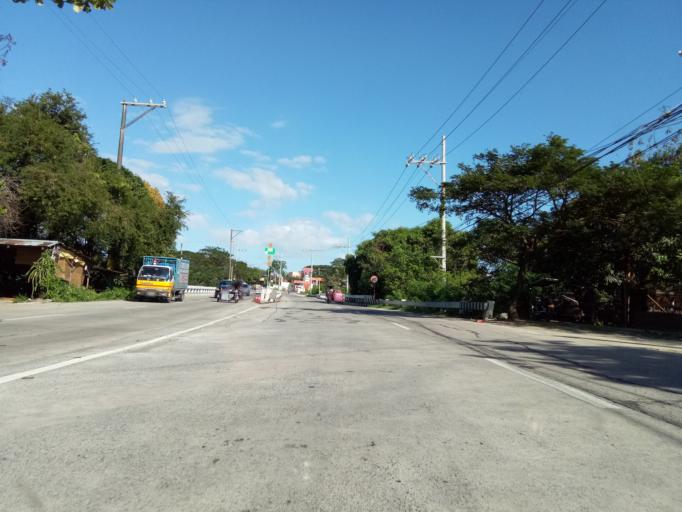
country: PH
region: Calabarzon
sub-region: Province of Cavite
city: Dasmarinas
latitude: 14.3497
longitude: 120.9704
